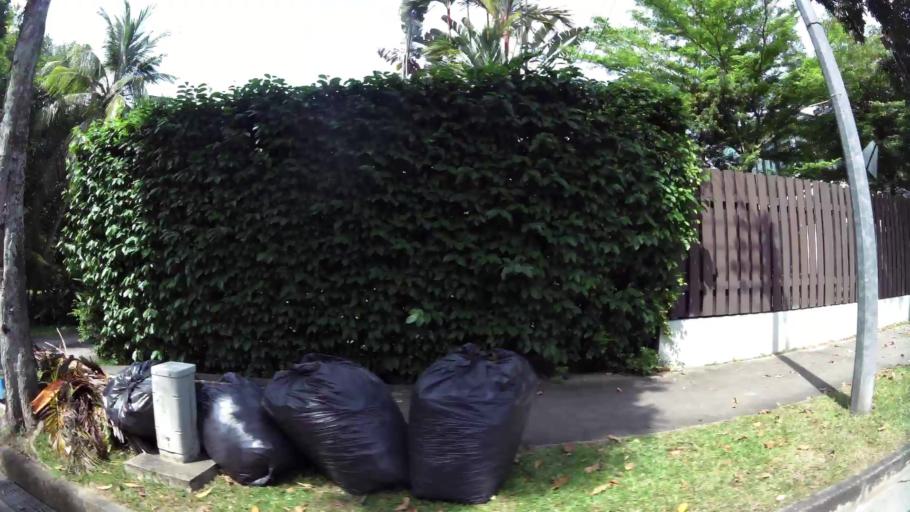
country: SG
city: Singapore
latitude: 1.3417
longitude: 103.7875
